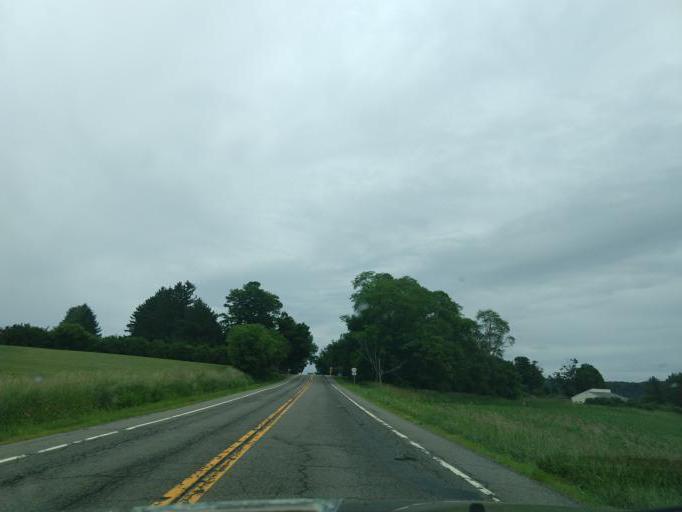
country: US
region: New York
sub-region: Tompkins County
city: Dryden
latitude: 42.4882
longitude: -76.2644
